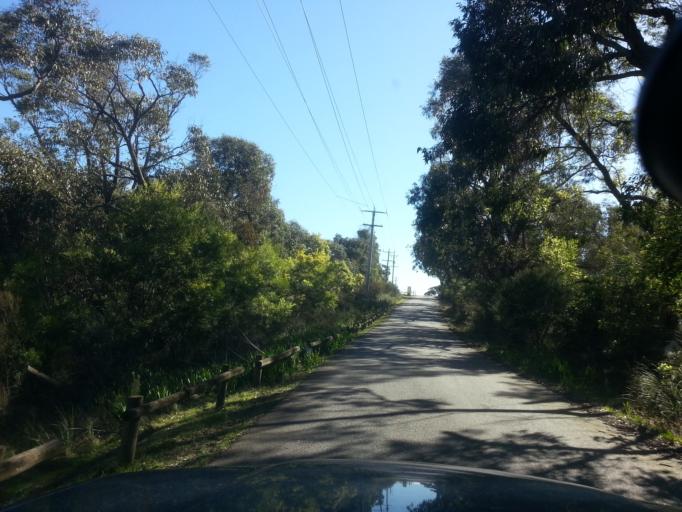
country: AU
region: Victoria
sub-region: Cardinia
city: Beaconsfield Upper
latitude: -37.9664
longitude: 145.3877
